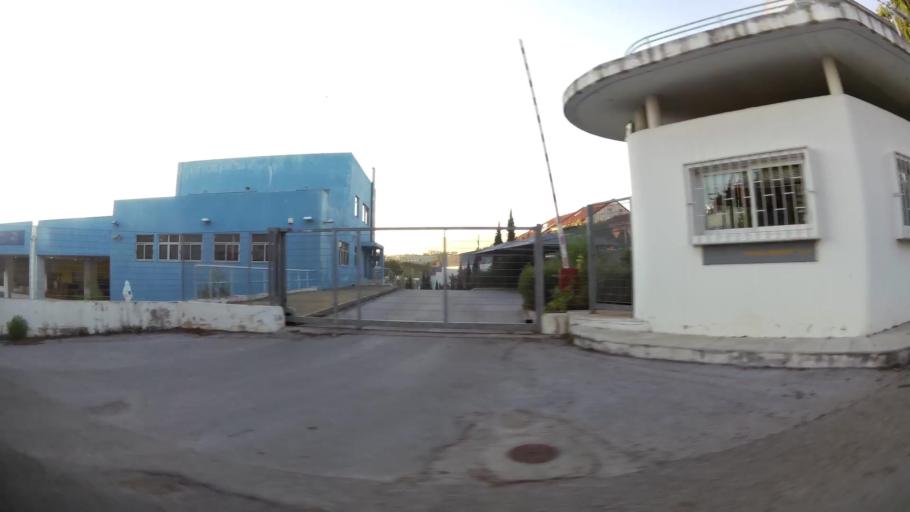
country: GR
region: Attica
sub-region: Nomarchia Anatolikis Attikis
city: Kryoneri
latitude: 38.1444
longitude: 23.8422
